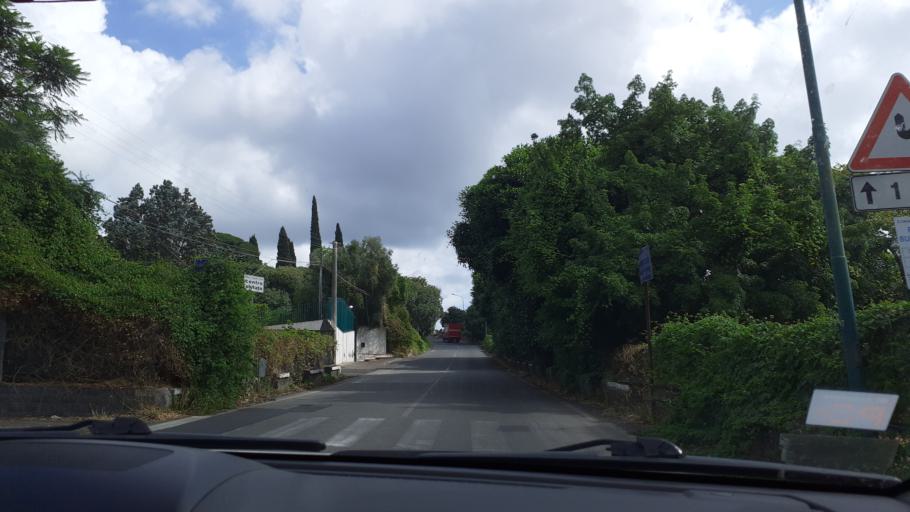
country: IT
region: Sicily
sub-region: Catania
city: Carrubazza-Motta
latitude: 37.5528
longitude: 15.1076
